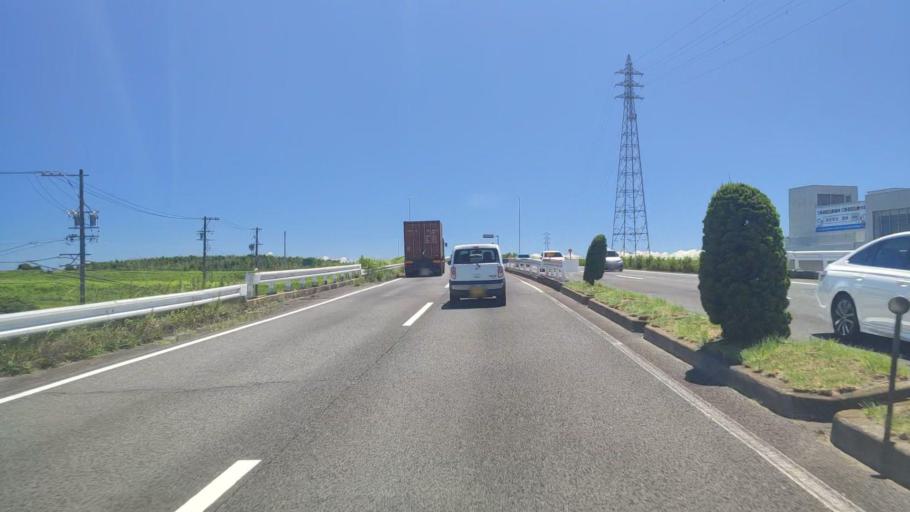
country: JP
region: Mie
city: Suzuka
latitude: 34.9105
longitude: 136.6051
